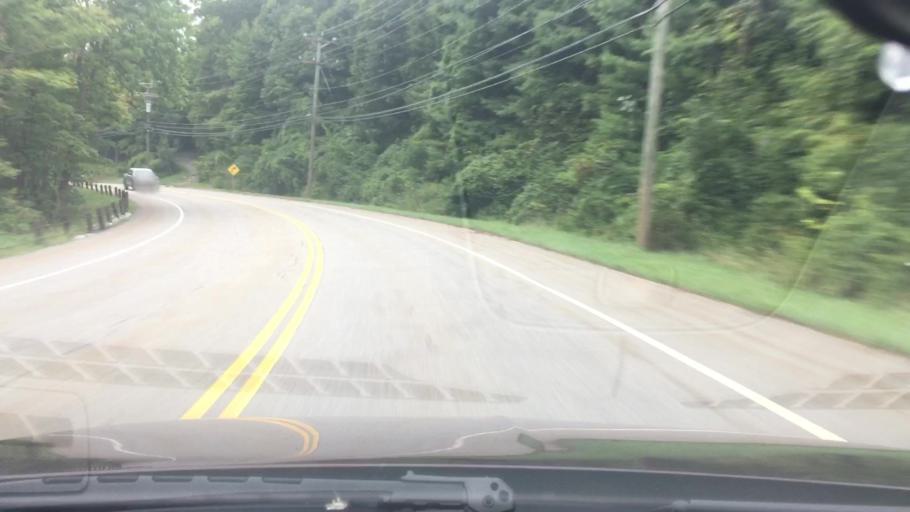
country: US
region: Connecticut
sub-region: Litchfield County
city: Litchfield
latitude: 41.8464
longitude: -73.3197
